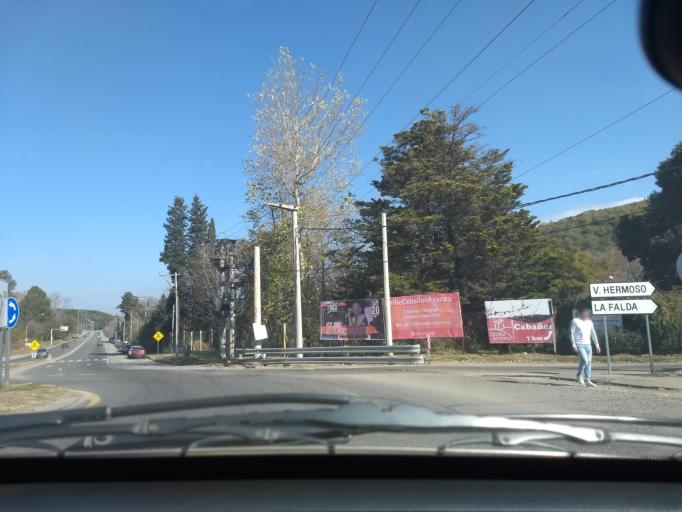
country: AR
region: Cordoba
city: Rio Ceballos
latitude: -31.1604
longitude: -64.3012
